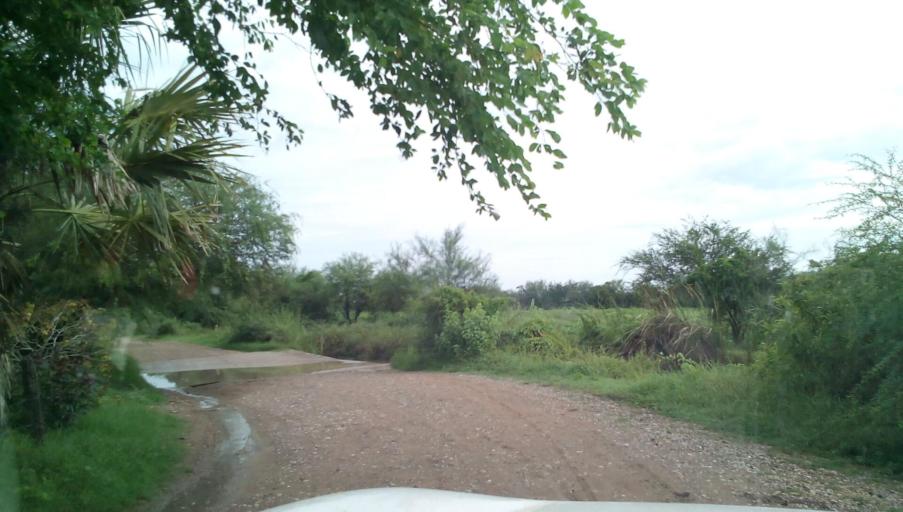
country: MX
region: Veracruz
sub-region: Panuco
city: Guayalejo
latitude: 22.3251
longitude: -98.3347
